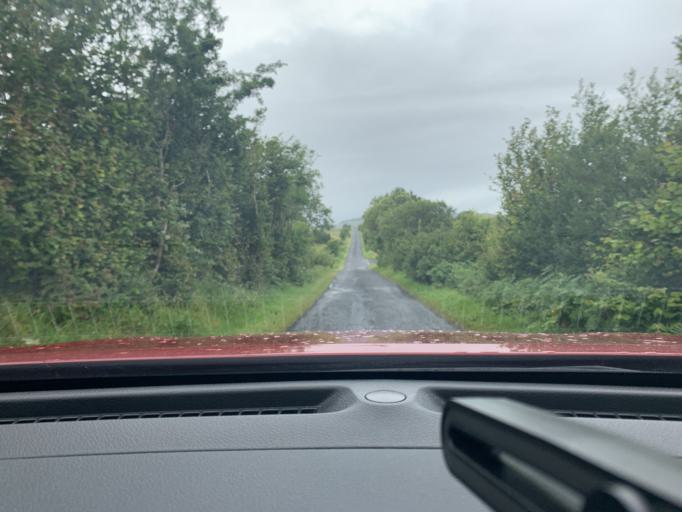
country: GB
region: Northern Ireland
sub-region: Fermanagh District
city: Enniskillen
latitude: 54.2551
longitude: -7.8328
